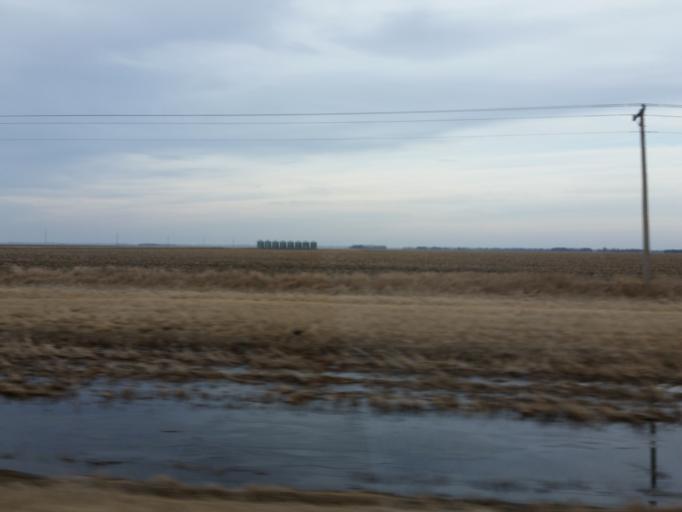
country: US
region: North Dakota
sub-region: Cass County
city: Casselton
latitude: 47.1641
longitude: -97.2175
